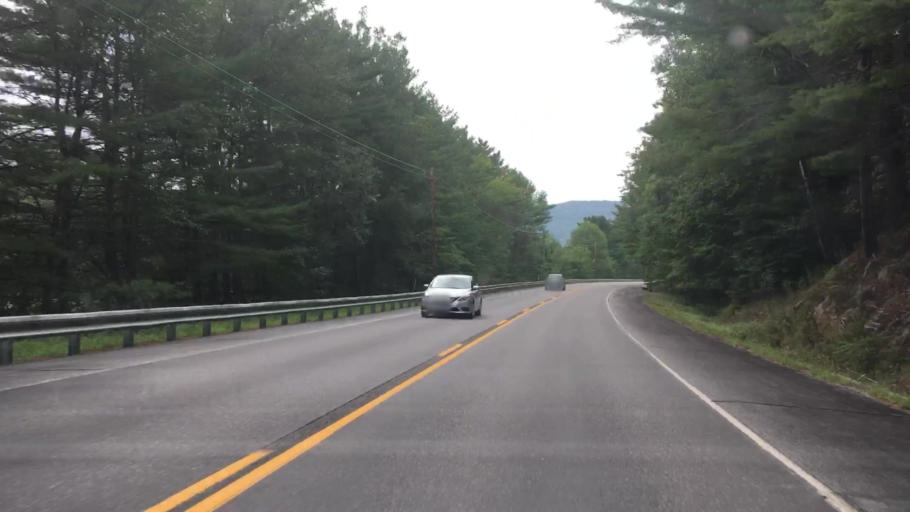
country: US
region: Maine
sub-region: Oxford County
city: Bethel
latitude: 44.4860
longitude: -70.7593
